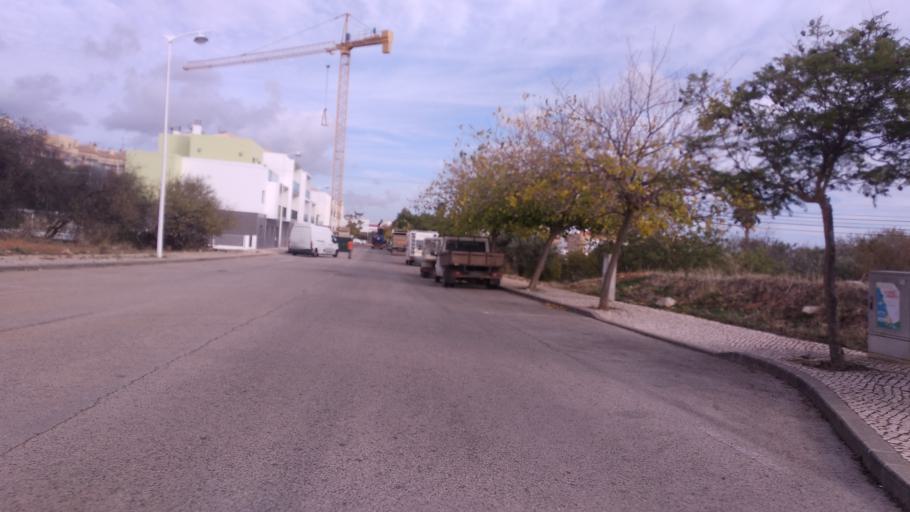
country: PT
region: Faro
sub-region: Sao Bras de Alportel
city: Sao Bras de Alportel
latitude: 37.1524
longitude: -7.8974
